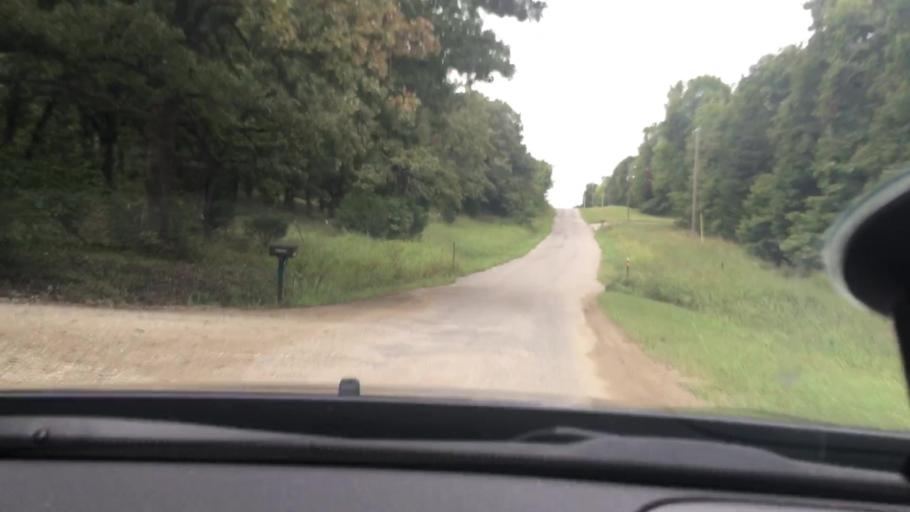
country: US
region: Oklahoma
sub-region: Pontotoc County
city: Byng
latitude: 34.8120
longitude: -96.5474
